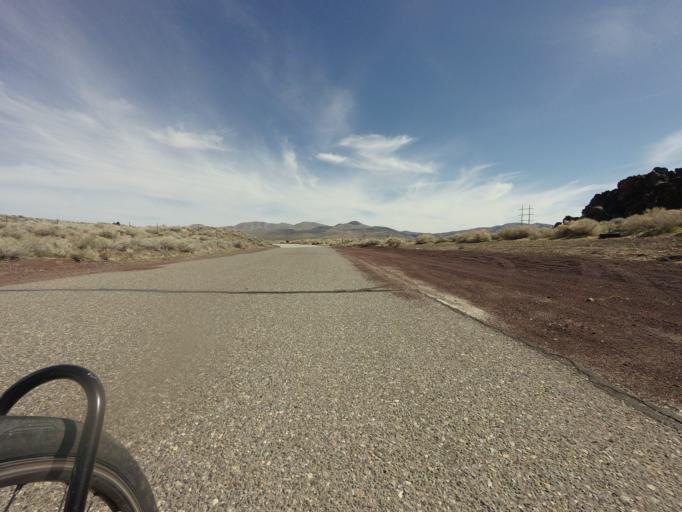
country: US
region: California
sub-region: Kern County
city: Inyokern
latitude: 35.9771
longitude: -117.9207
